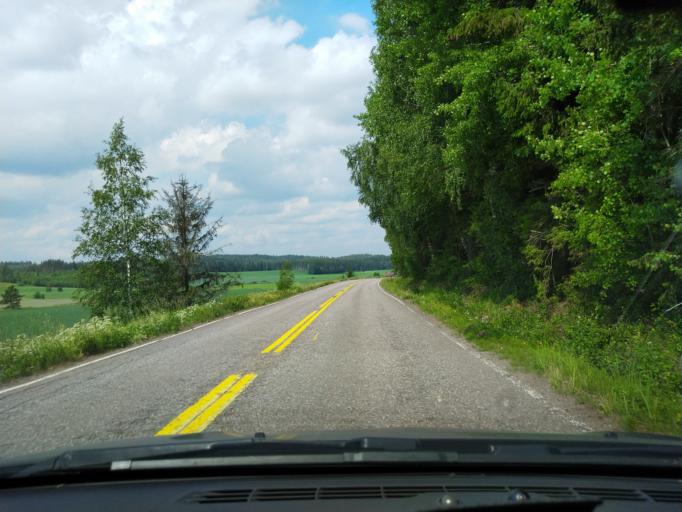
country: FI
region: Uusimaa
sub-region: Helsinki
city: Saukkola
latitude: 60.4325
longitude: 24.0659
